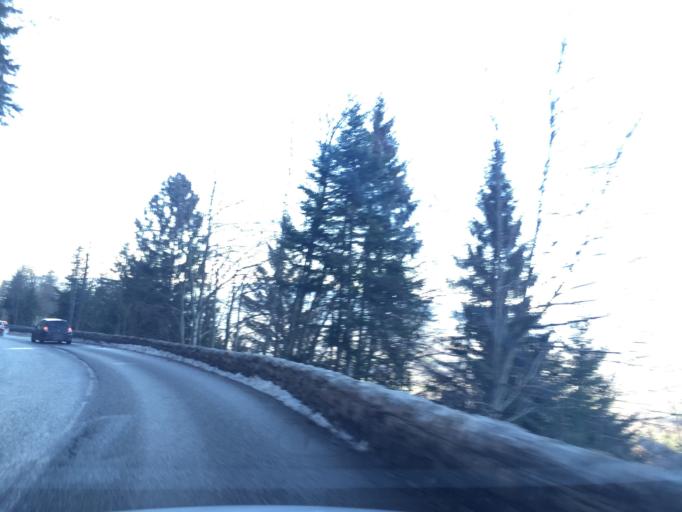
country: FR
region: Rhone-Alpes
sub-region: Departement de la Haute-Savoie
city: Cusy
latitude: 45.7037
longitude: 6.0024
